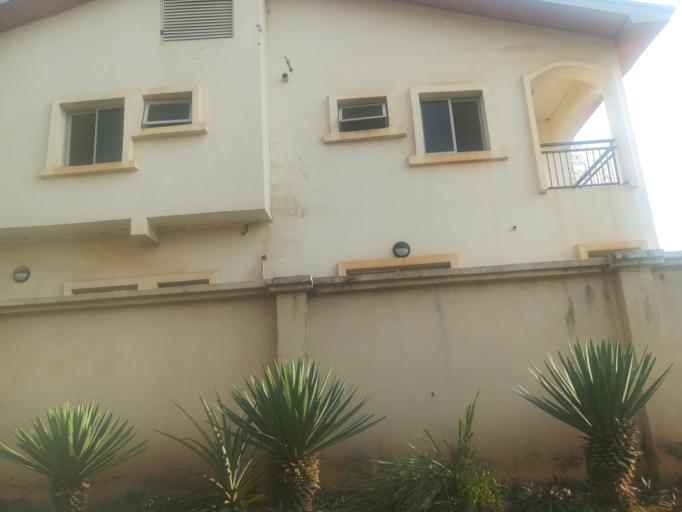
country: NG
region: Abuja Federal Capital Territory
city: Abuja
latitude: 9.0529
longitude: 7.4516
